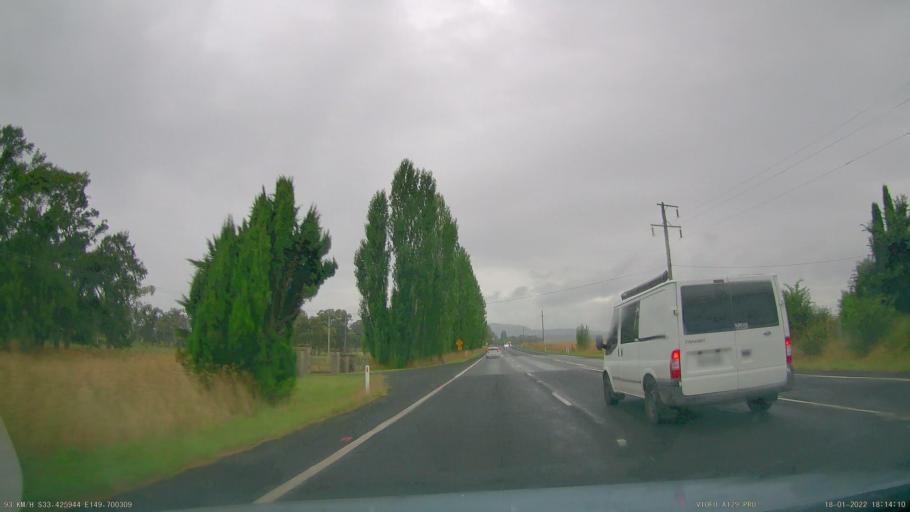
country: AU
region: New South Wales
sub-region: Bathurst Regional
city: Kelso
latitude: -33.4260
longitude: 149.7006
